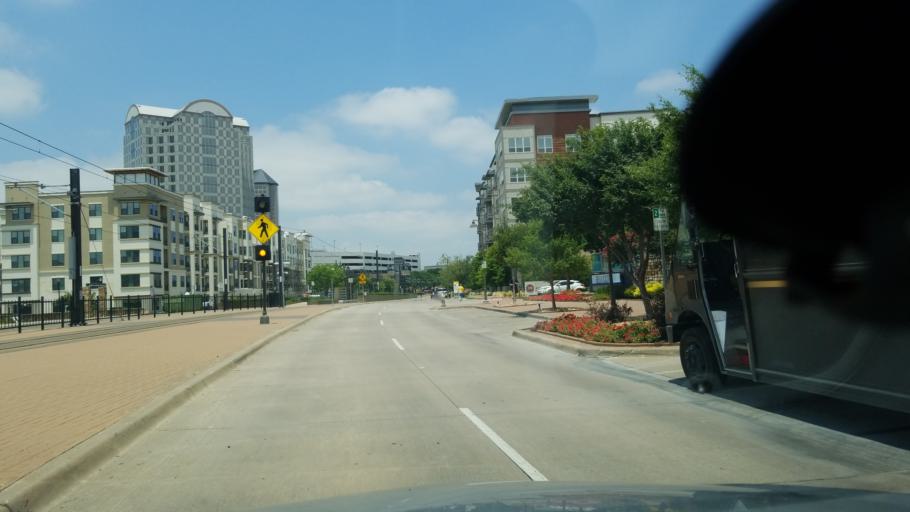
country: US
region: Texas
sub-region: Dallas County
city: Irving
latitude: 32.8676
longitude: -96.9323
